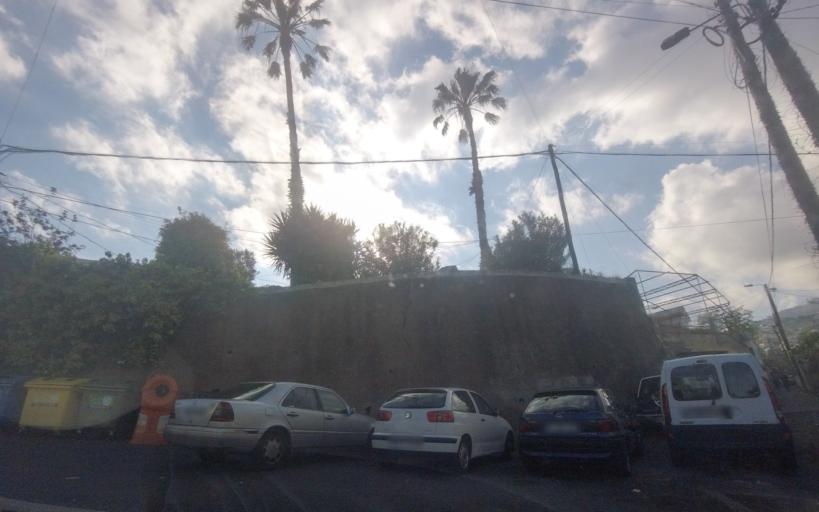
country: PT
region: Madeira
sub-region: Funchal
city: Nossa Senhora do Monte
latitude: 32.6568
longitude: -16.9324
